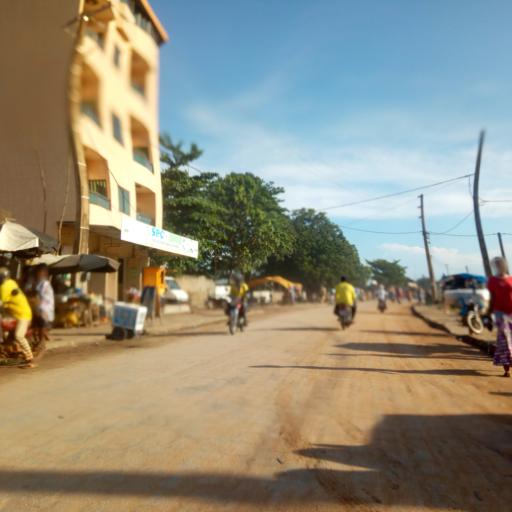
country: BJ
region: Atlantique
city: Hevie
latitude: 6.3912
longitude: 2.2721
